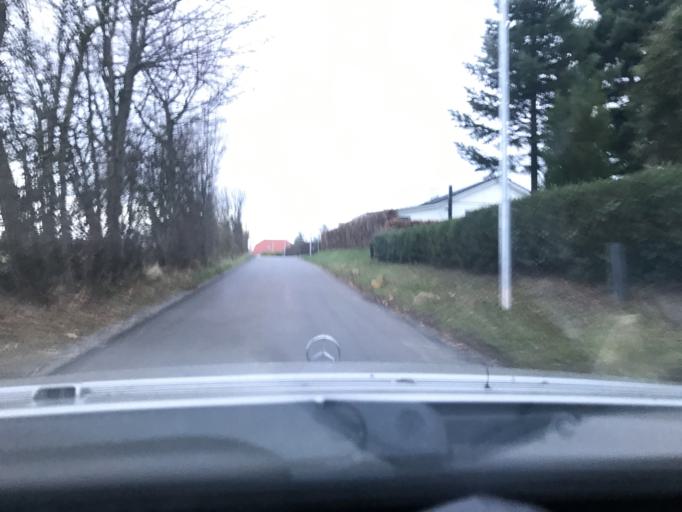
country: DK
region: South Denmark
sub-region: Sonderborg Kommune
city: Nordborg
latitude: 55.0560
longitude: 9.7011
